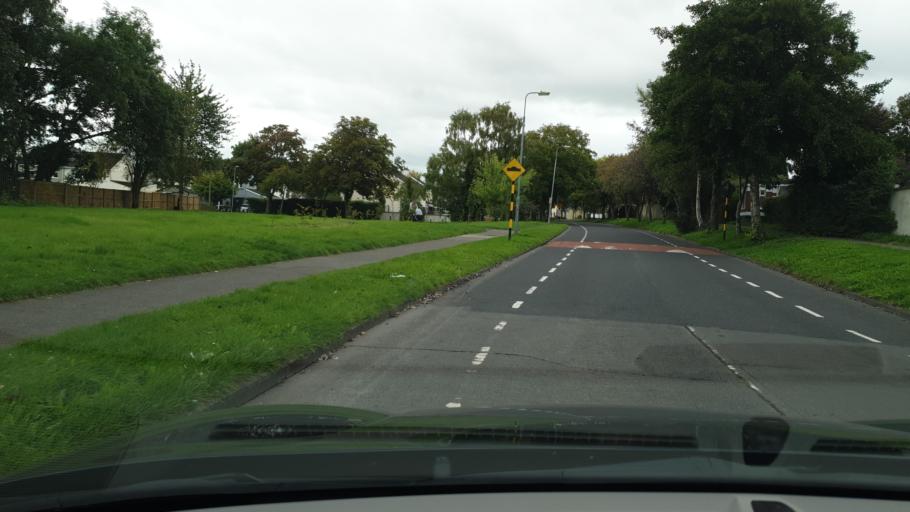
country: IE
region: Leinster
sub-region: Kildare
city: Naas
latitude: 53.2271
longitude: -6.6550
